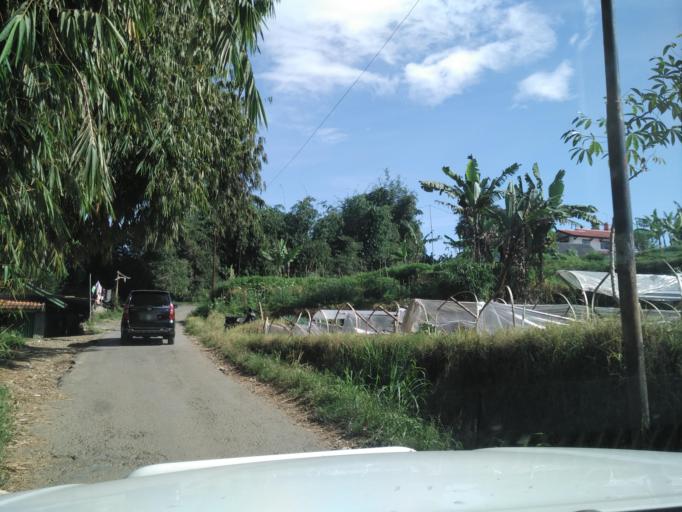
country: ID
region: West Java
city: Sukabumi
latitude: -6.7725
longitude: 107.0549
